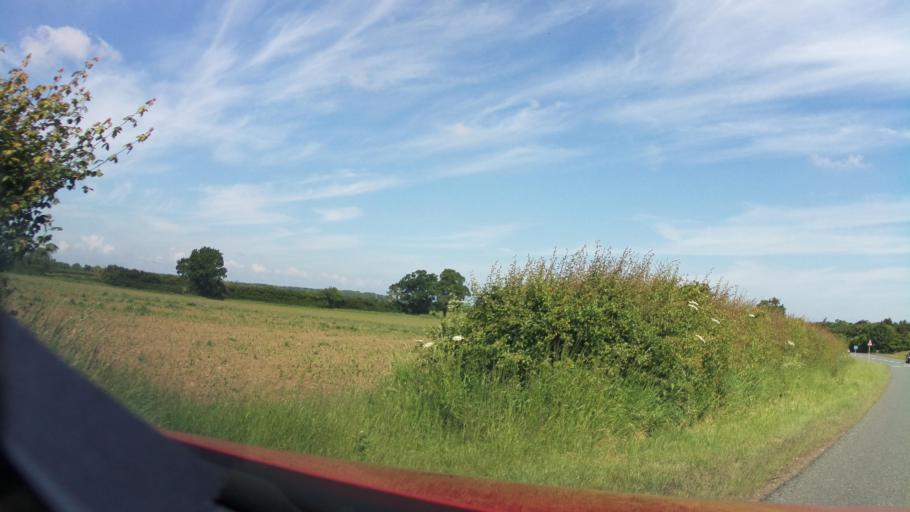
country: GB
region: England
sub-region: Lincolnshire
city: Skellingthorpe
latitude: 53.1635
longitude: -0.6387
